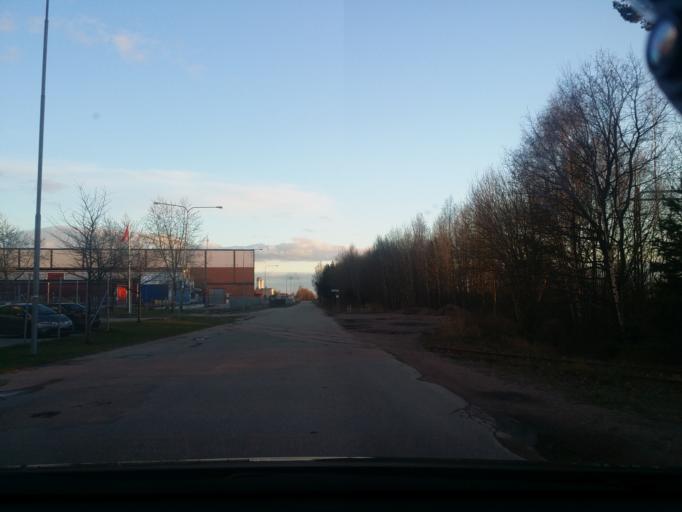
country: SE
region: Vaestmanland
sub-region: Vasteras
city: Hokasen
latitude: 59.6408
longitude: 16.5791
